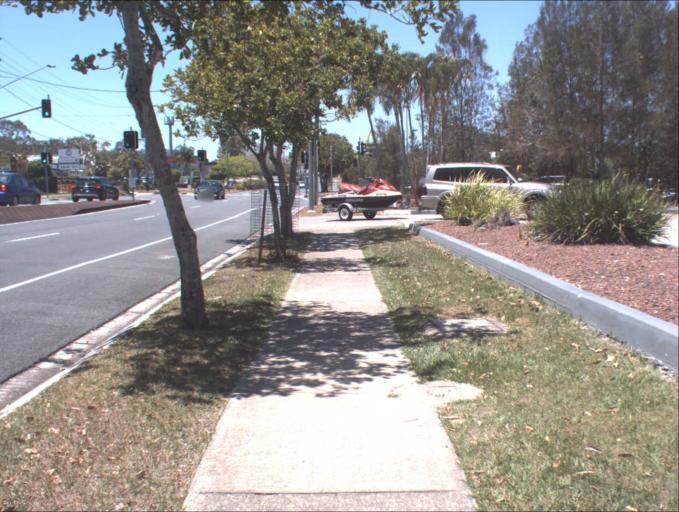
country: AU
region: Queensland
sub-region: Logan
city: Slacks Creek
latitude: -27.6631
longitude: 153.1776
